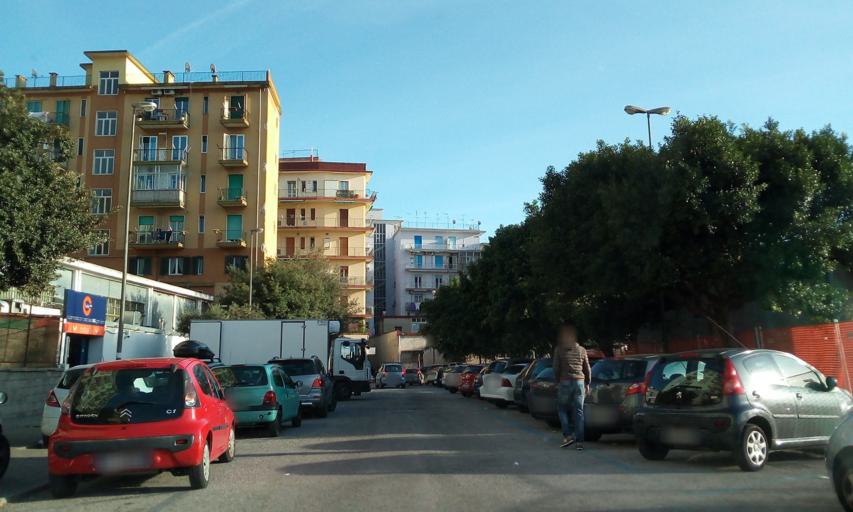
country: IT
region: Campania
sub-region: Provincia di Salerno
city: Salerno
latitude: 40.6750
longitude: 14.7765
